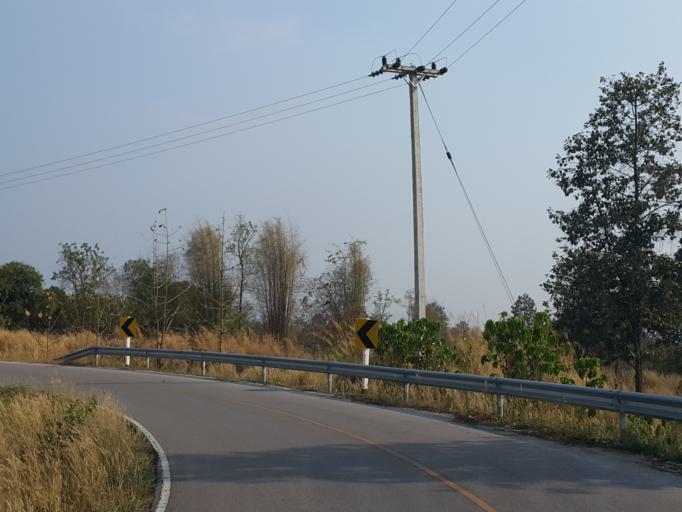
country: TH
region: Lampang
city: Chae Hom
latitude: 18.7261
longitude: 99.5541
